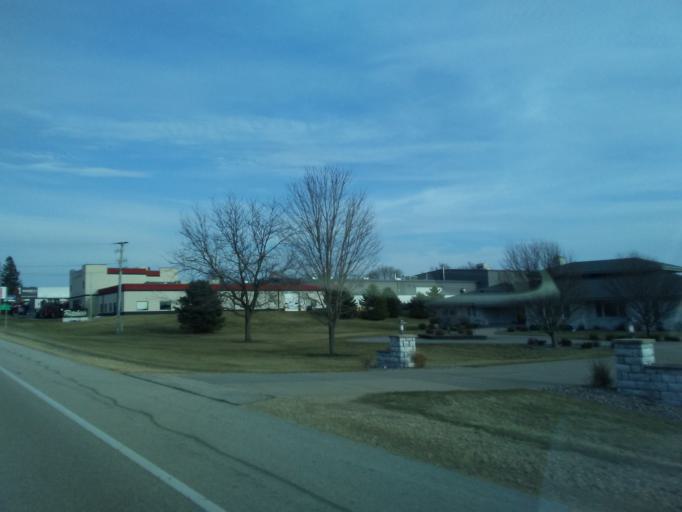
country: US
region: Wisconsin
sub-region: Iowa County
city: Mineral Point
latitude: 42.9672
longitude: -90.3387
